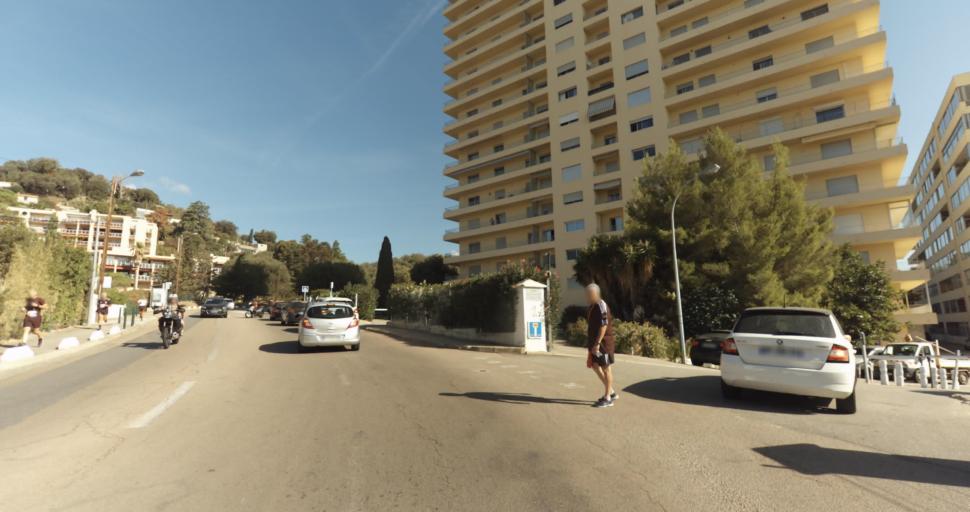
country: FR
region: Corsica
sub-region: Departement de la Corse-du-Sud
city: Ajaccio
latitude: 41.9208
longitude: 8.7302
